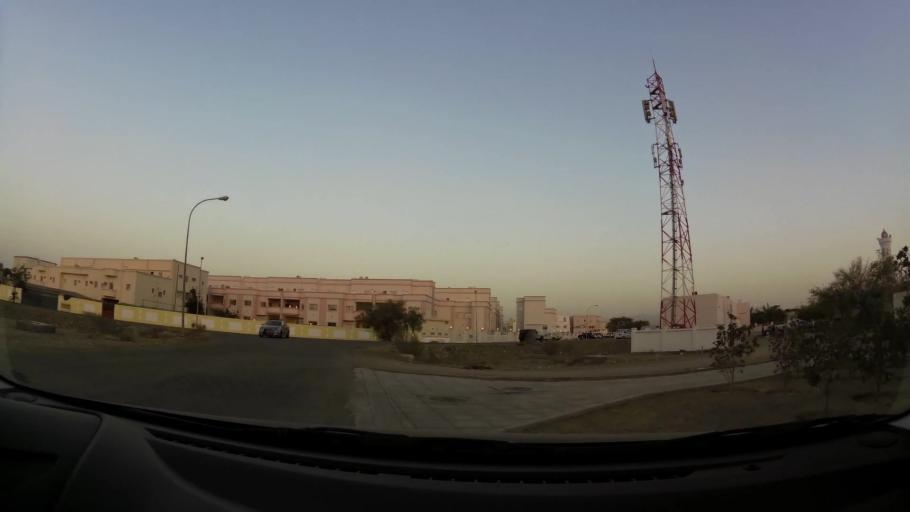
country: OM
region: Muhafazat Masqat
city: As Sib al Jadidah
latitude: 23.6444
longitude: 58.2147
